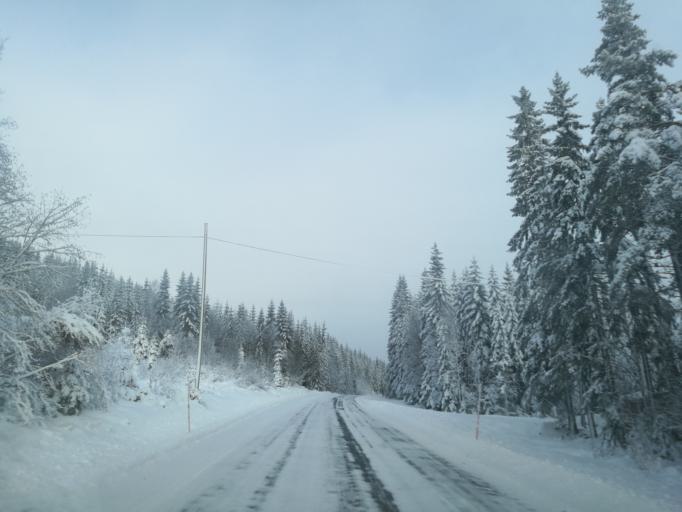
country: SE
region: Vaermland
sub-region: Torsby Kommun
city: Torsby
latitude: 60.5956
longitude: 12.7319
